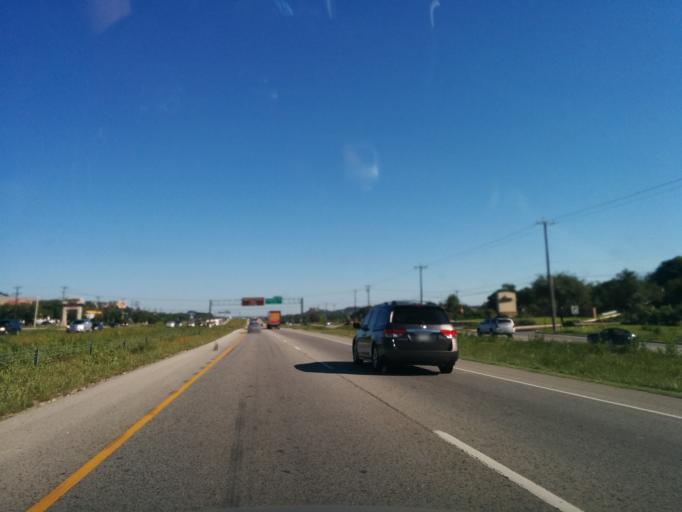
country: US
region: Texas
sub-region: Bexar County
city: Cross Mountain
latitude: 29.6179
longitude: -98.6072
